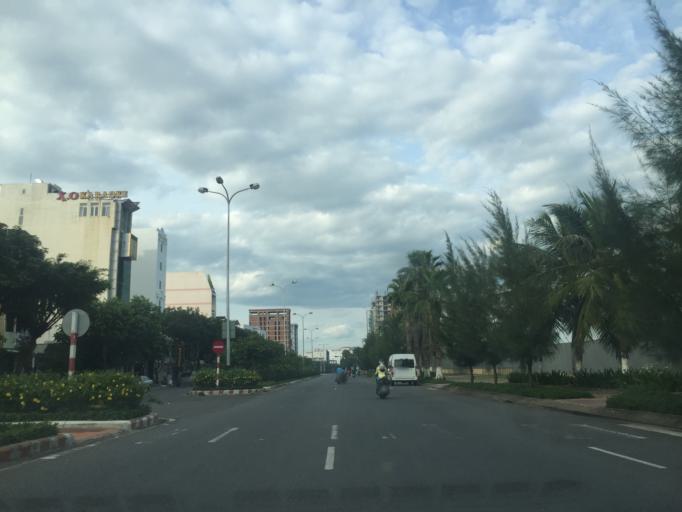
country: VN
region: Da Nang
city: Da Nang
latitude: 16.0820
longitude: 108.2122
